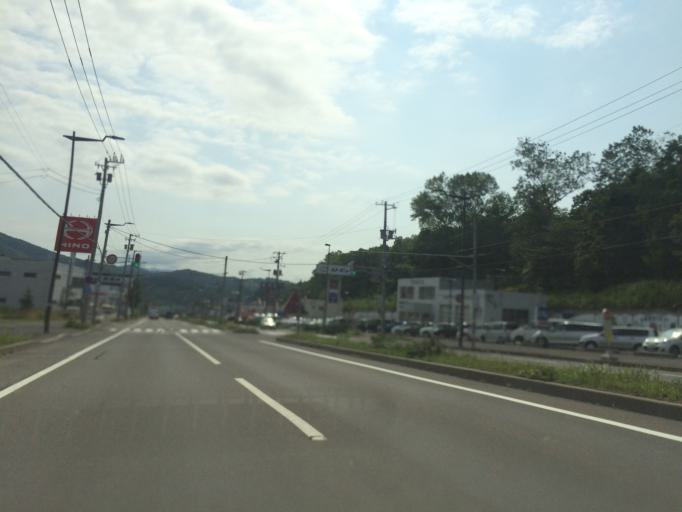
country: JP
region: Hokkaido
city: Otaru
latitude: 43.2161
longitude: 140.9425
